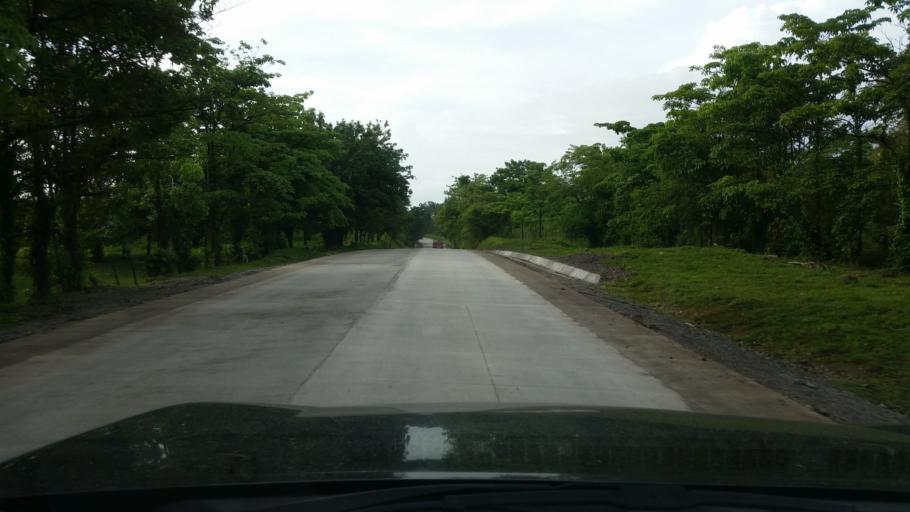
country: NI
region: Matagalpa
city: Rio Blanco
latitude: 13.0911
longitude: -85.0625
